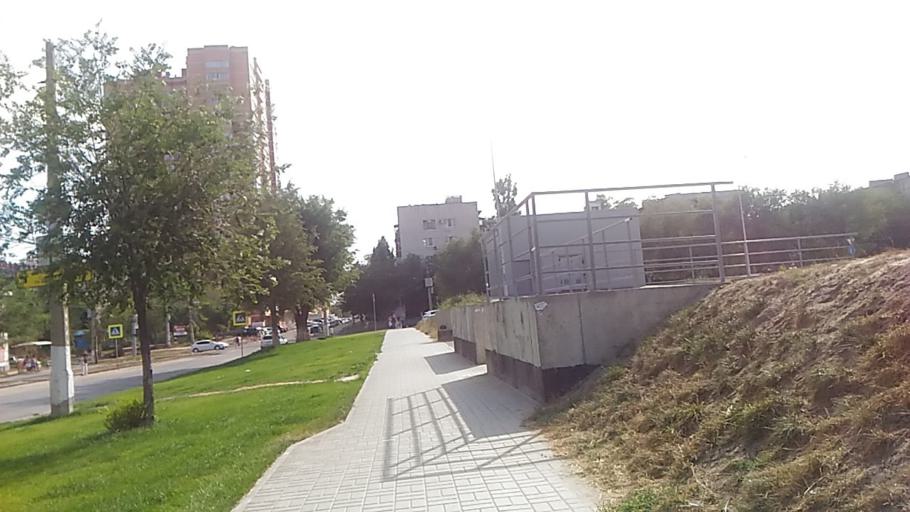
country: RU
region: Volgograd
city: Volgograd
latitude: 48.6920
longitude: 44.4959
